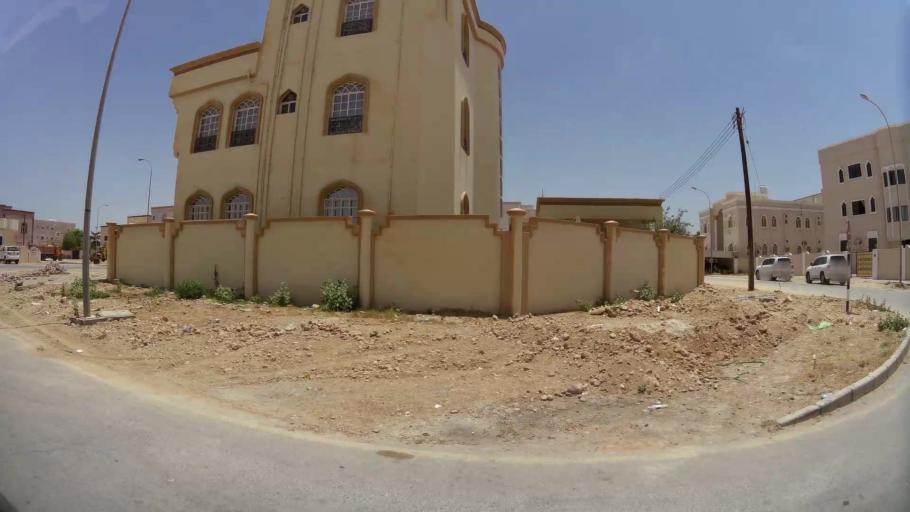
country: OM
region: Zufar
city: Salalah
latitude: 17.0733
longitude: 54.1597
